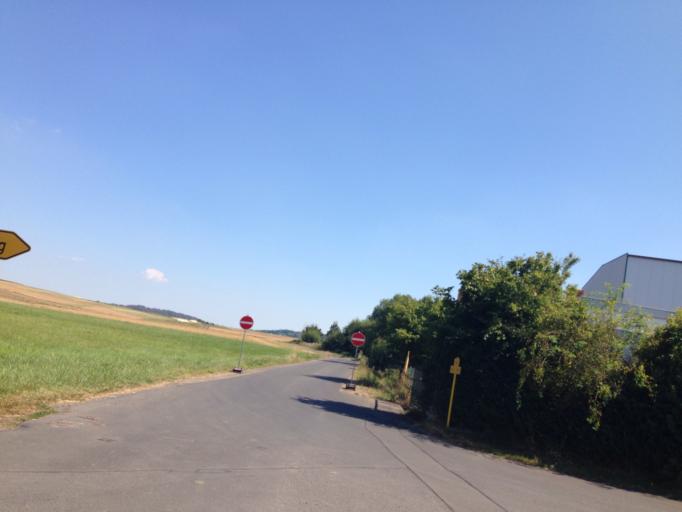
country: DE
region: Hesse
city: Staufenberg
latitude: 50.6620
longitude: 8.7595
